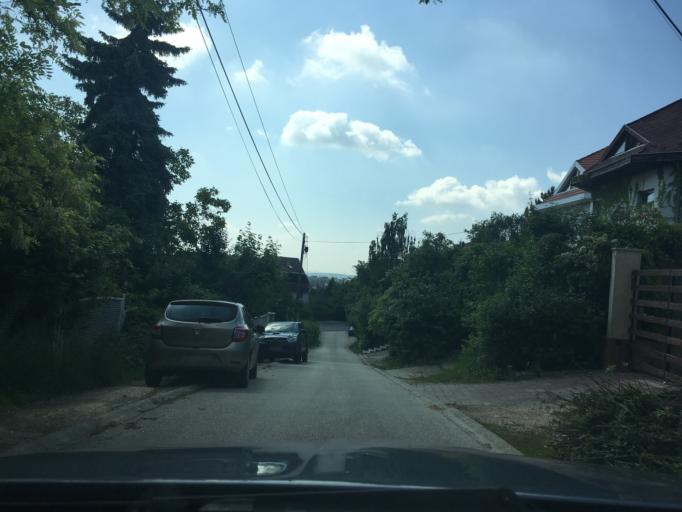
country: HU
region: Budapest
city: Budapest XII. keruelet
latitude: 47.4795
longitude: 18.9915
